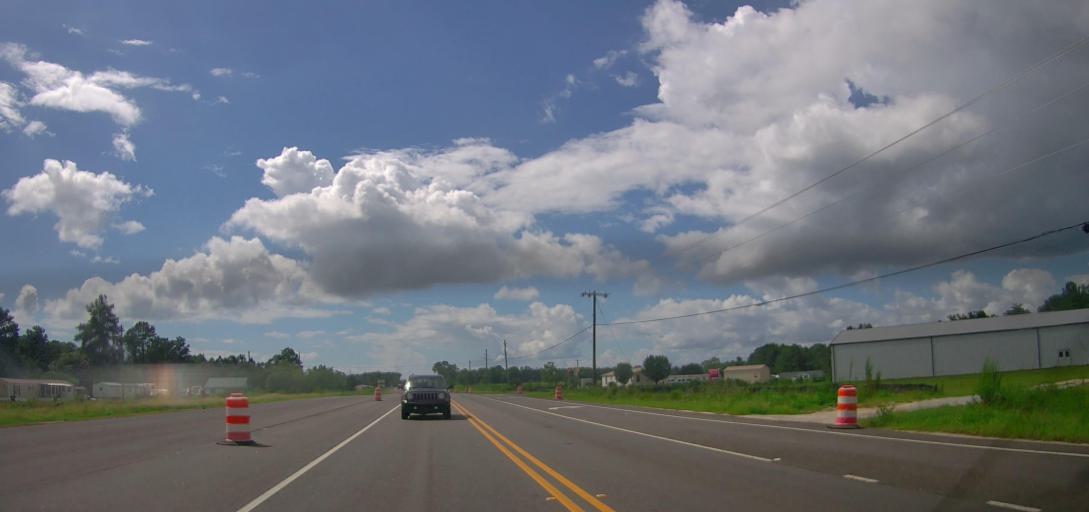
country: US
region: Georgia
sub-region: Coffee County
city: Douglas
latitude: 31.5414
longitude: -82.9275
